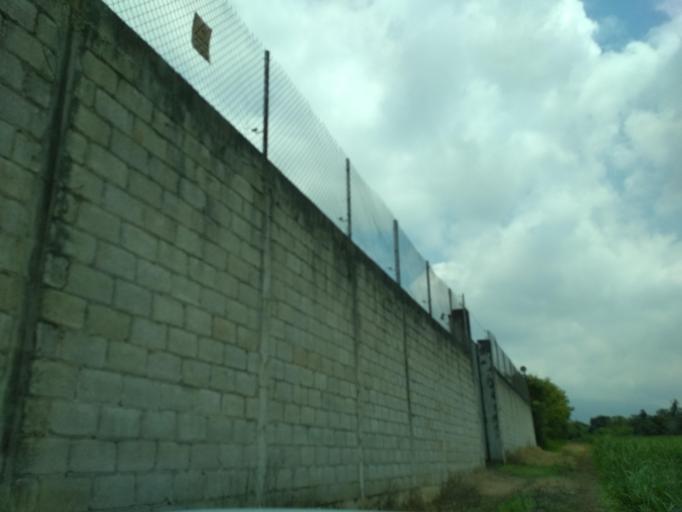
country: MX
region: Veracruz
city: Atzacan
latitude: 18.8795
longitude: -97.0769
